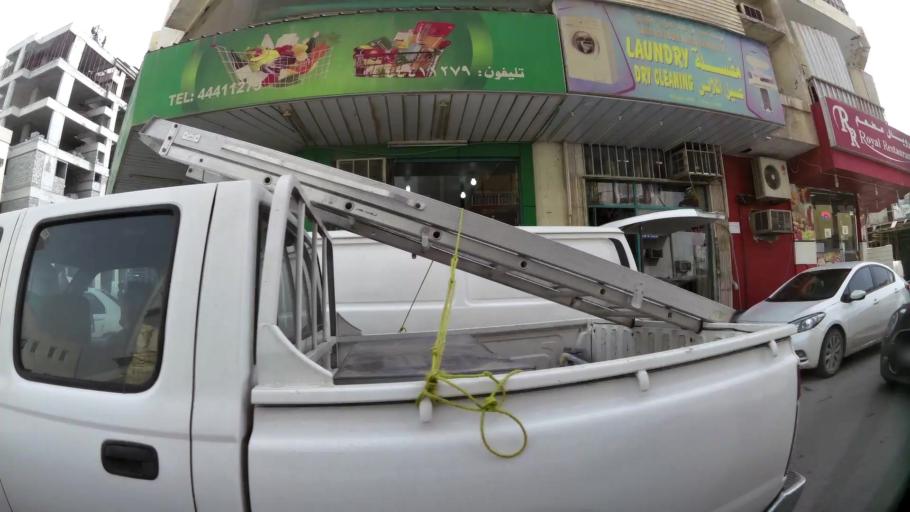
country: QA
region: Baladiyat ad Dawhah
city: Doha
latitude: 25.2776
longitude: 51.5499
